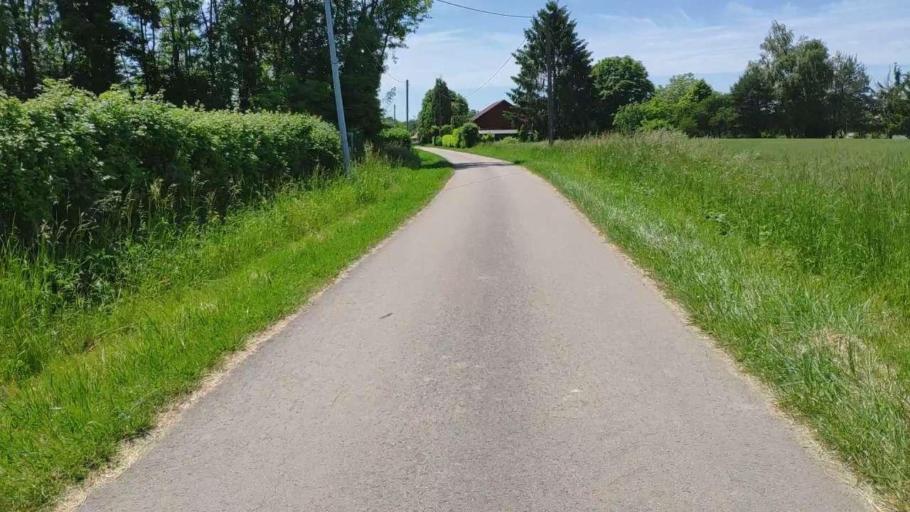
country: FR
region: Franche-Comte
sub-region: Departement du Jura
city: Bletterans
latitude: 46.7998
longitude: 5.3974
